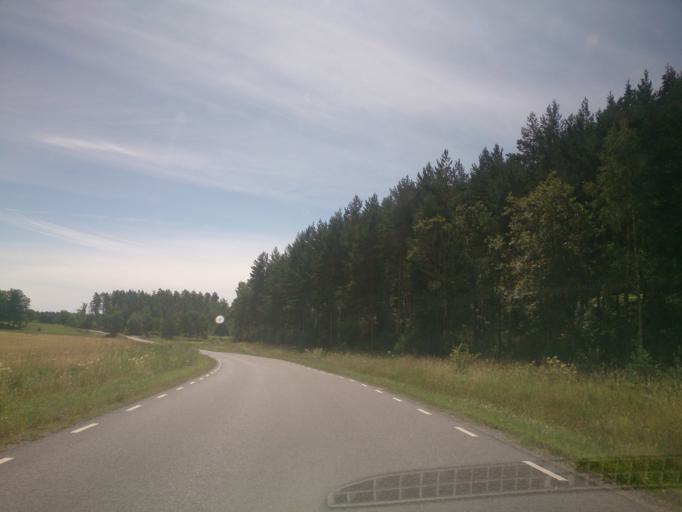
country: SE
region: OEstergoetland
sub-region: Valdemarsviks Kommun
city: Valdemarsvik
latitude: 58.3409
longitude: 16.6131
